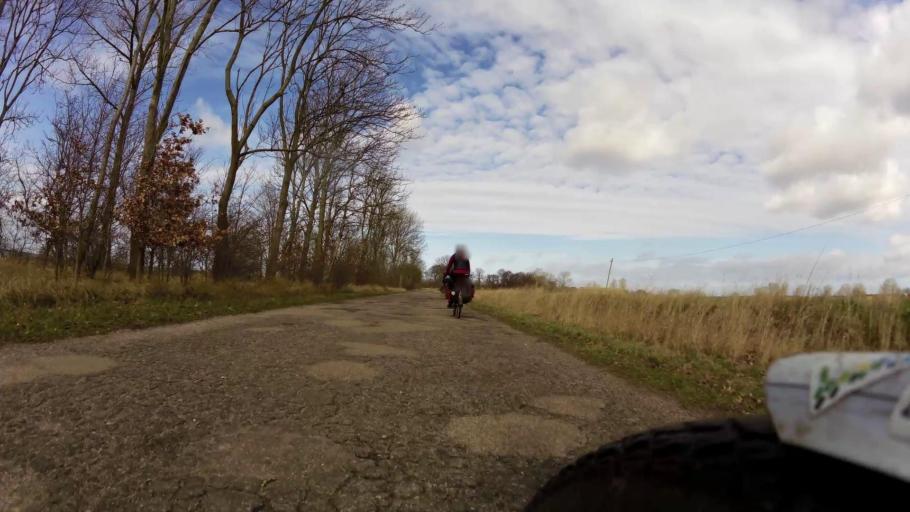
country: PL
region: West Pomeranian Voivodeship
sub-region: Powiat kamienski
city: Kamien Pomorski
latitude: 53.9875
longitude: 14.7687
